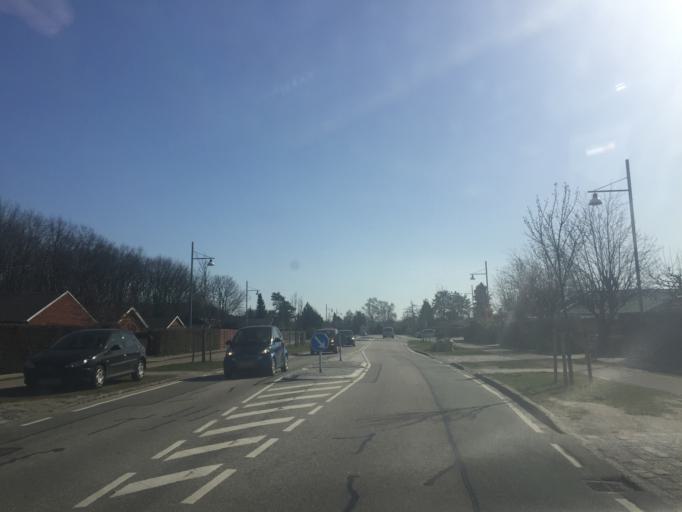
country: DK
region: Capital Region
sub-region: Glostrup Kommune
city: Glostrup
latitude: 55.6776
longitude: 12.4093
